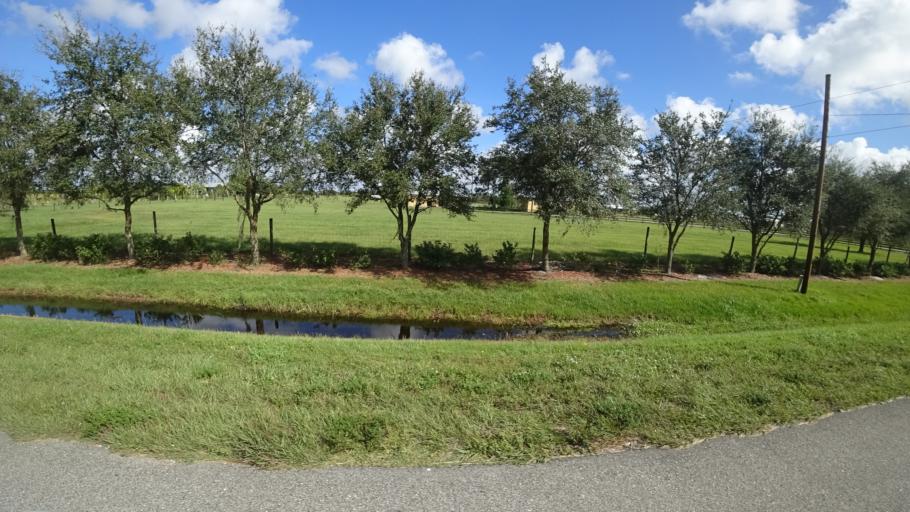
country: US
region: Florida
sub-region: Sarasota County
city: Lake Sarasota
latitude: 27.3618
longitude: -82.1982
